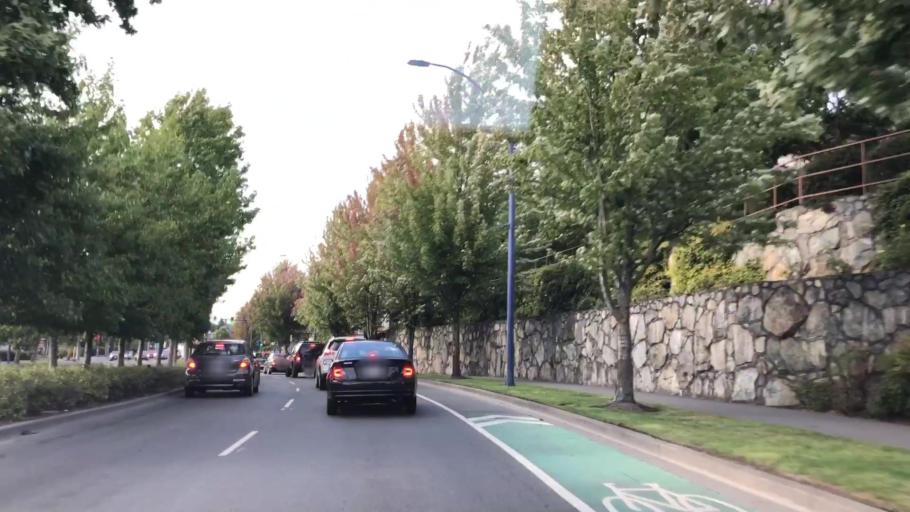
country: CA
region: British Columbia
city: Langford
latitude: 48.4606
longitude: -123.4972
